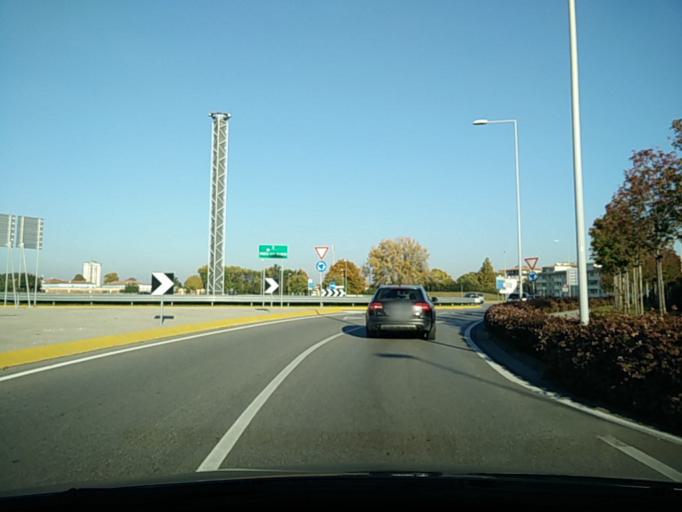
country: IT
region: Veneto
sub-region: Provincia di Treviso
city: Treviso
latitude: 45.6700
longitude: 12.2275
